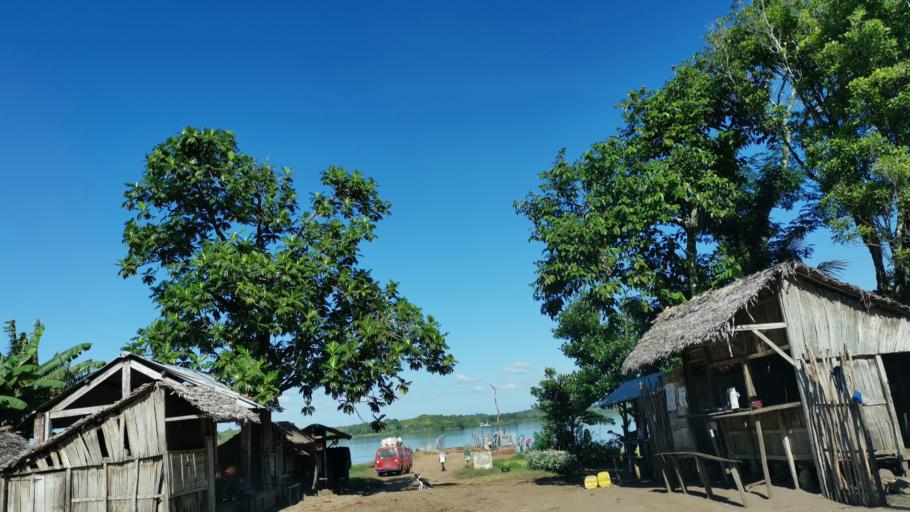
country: MG
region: Atsimo-Atsinanana
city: Vohipaho
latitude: -23.5986
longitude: 47.6120
